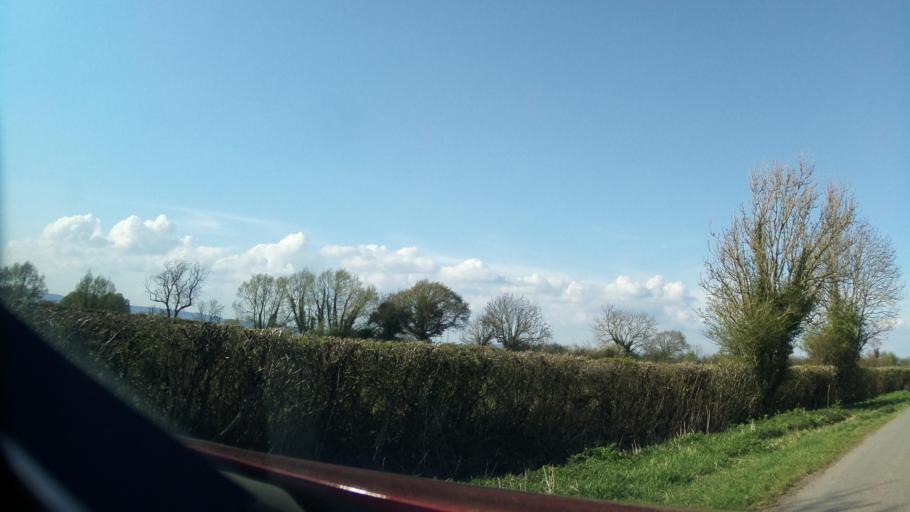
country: GB
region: England
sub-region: South Gloucestershire
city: Hill
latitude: 51.6457
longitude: -2.5408
